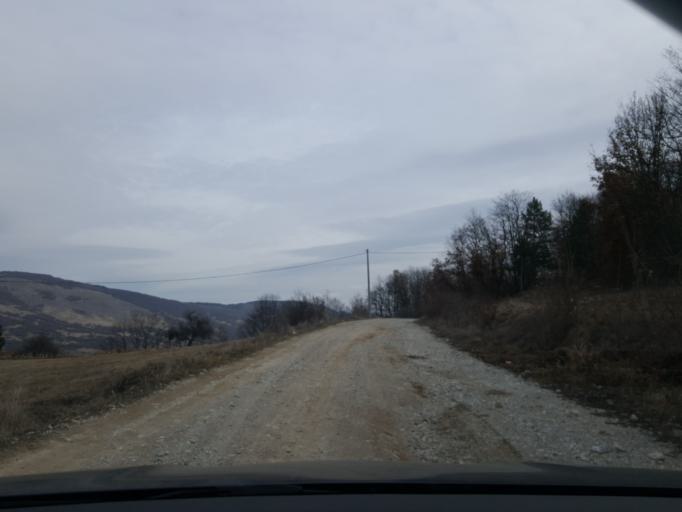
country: RS
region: Central Serbia
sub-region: Pirotski Okrug
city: Dimitrovgrad
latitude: 43.0053
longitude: 22.7513
